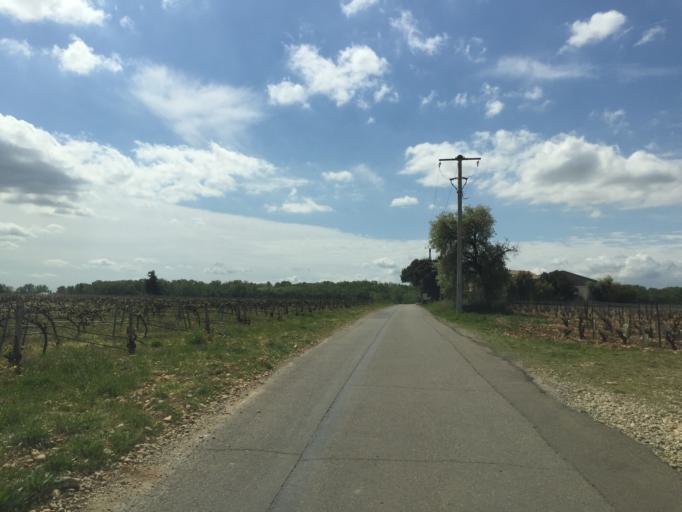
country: FR
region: Provence-Alpes-Cote d'Azur
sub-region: Departement du Vaucluse
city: Chateauneuf-du-Pape
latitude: 44.0461
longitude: 4.8294
